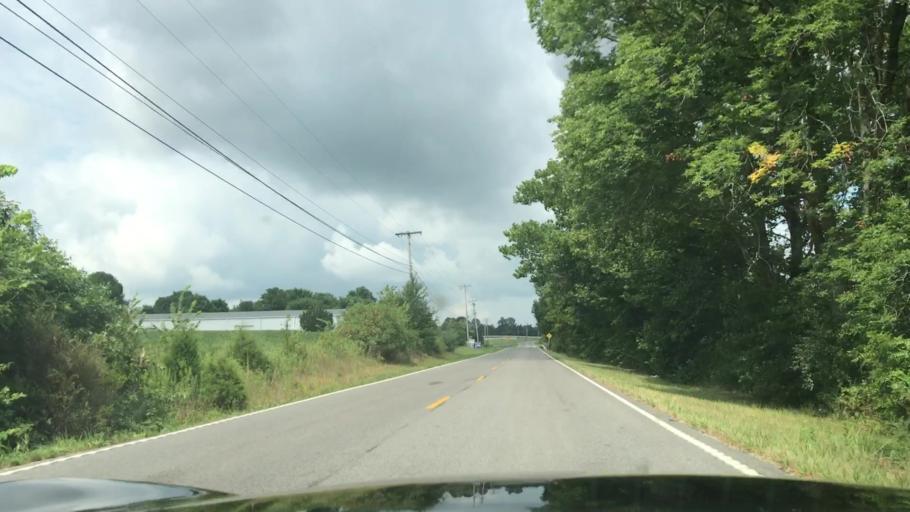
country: US
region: Kentucky
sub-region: Muhlenberg County
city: Greenville
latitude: 37.1976
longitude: -87.1216
